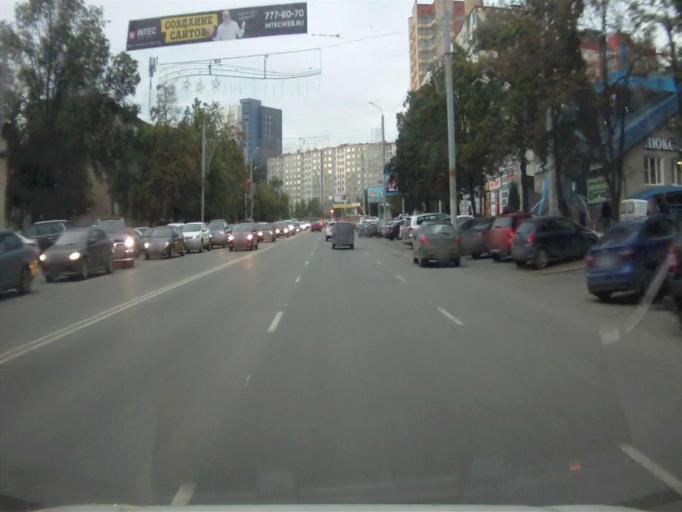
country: RU
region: Chelyabinsk
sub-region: Gorod Chelyabinsk
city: Chelyabinsk
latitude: 55.1554
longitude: 61.3815
